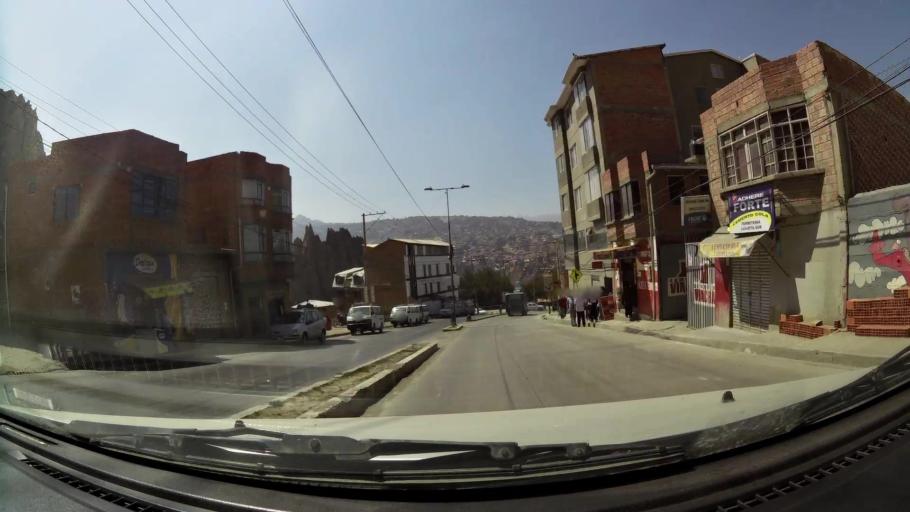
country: BO
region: La Paz
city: La Paz
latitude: -16.5241
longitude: -68.1227
